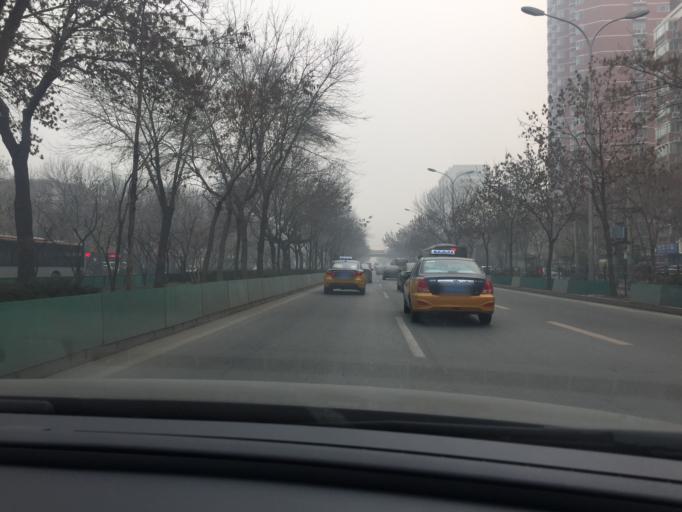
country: CN
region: Beijing
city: Qinghe
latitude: 40.0056
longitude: 116.3461
